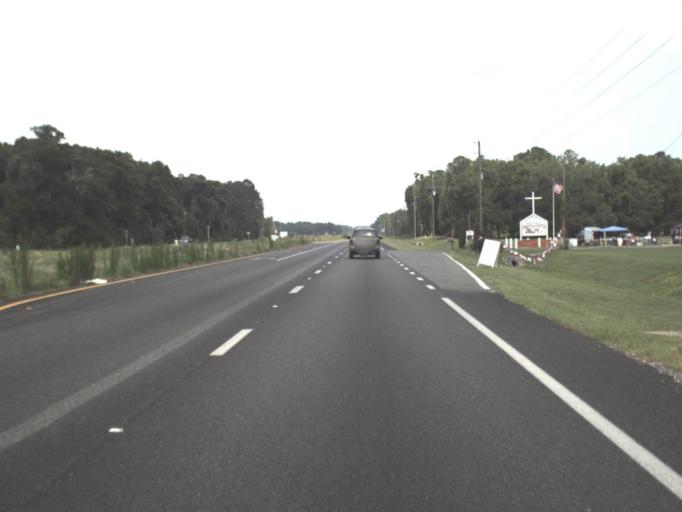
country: US
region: Florida
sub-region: Levy County
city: Williston
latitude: 29.3943
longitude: -82.4838
